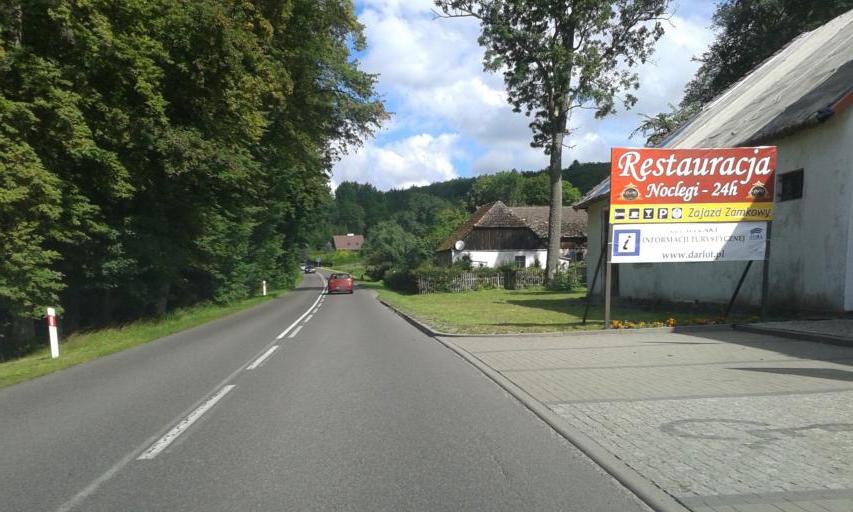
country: PL
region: West Pomeranian Voivodeship
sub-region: Powiat koszalinski
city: Polanow
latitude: 54.2160
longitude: 16.7016
